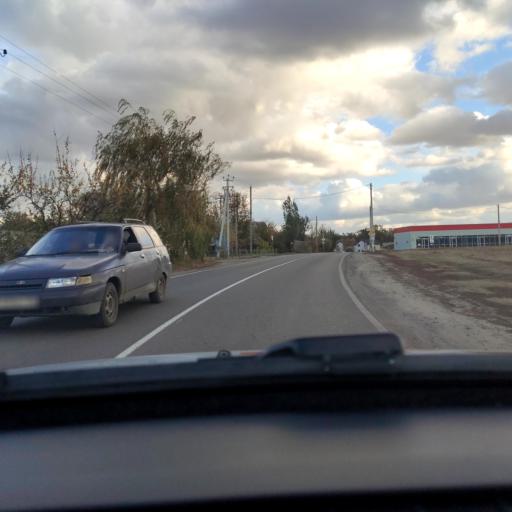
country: RU
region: Voronezj
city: Ramon'
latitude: 51.8269
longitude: 39.2547
